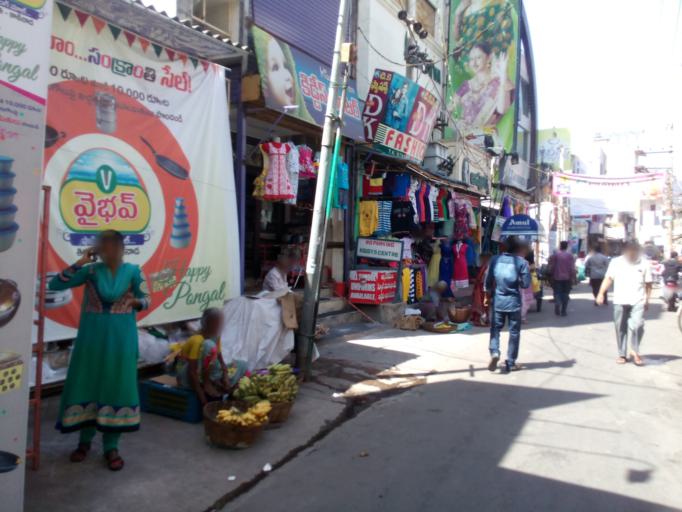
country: IN
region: Andhra Pradesh
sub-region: Chittoor
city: Tirupati
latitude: 13.6315
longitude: 79.4183
